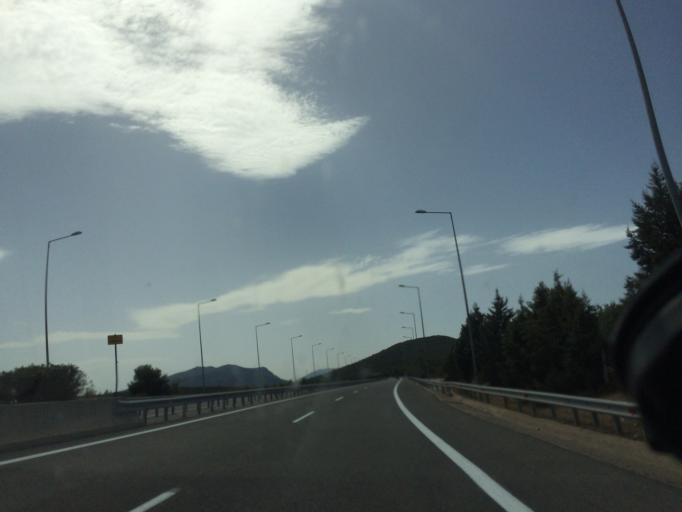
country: GR
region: Central Greece
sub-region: Nomos Voiotias
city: Akraifnia
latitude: 38.4304
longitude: 23.2293
